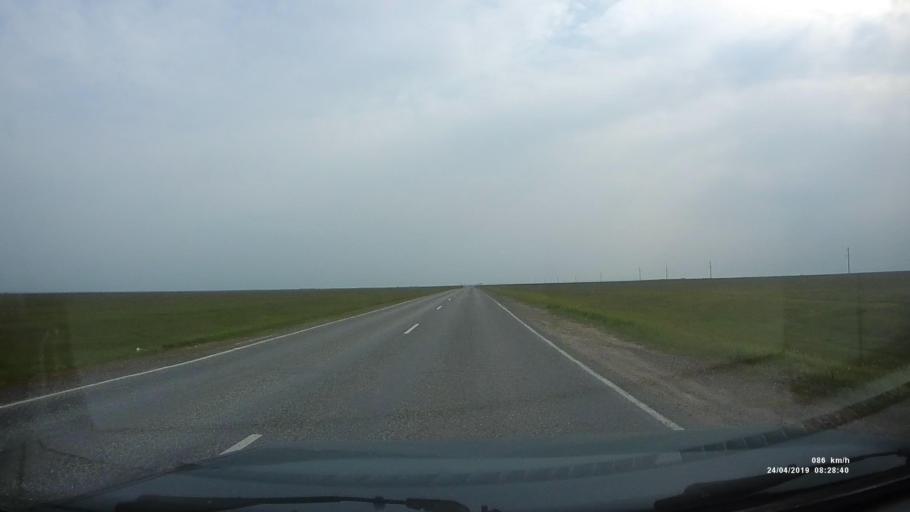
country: RU
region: Kalmykiya
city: Priyutnoye
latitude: 46.1463
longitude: 43.8192
